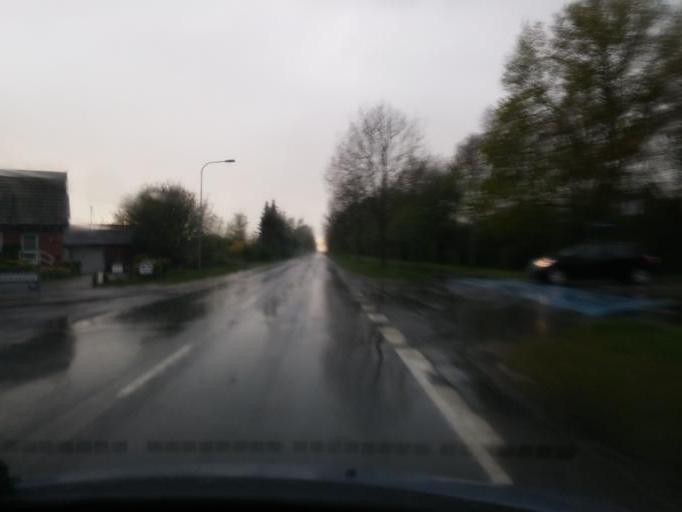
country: DK
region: South Denmark
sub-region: Odense Kommune
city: Bellinge
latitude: 55.3405
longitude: 10.2987
